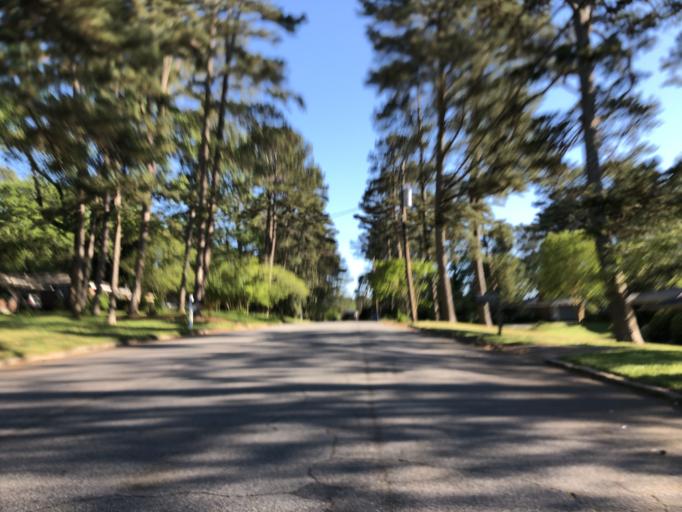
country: US
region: Georgia
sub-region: DeKalb County
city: North Decatur
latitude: 33.7943
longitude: -84.2988
